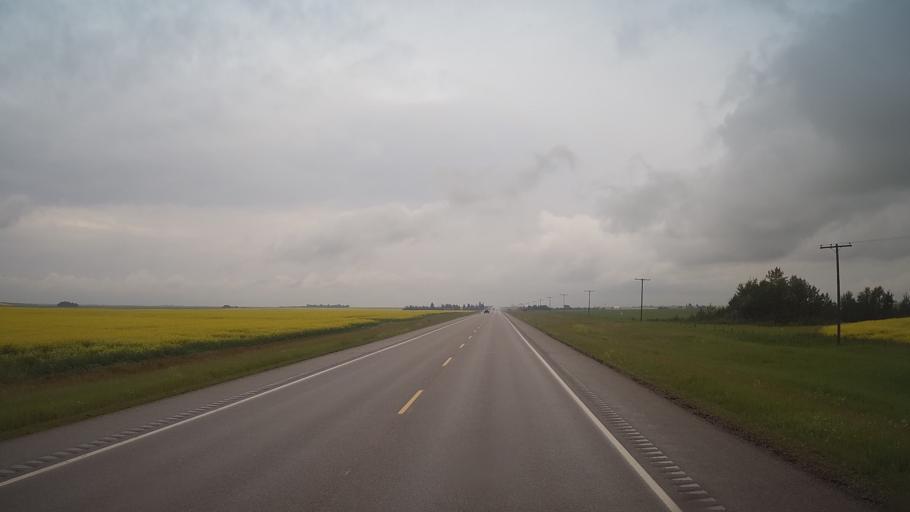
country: CA
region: Saskatchewan
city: Unity
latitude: 52.4349
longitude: -109.0111
